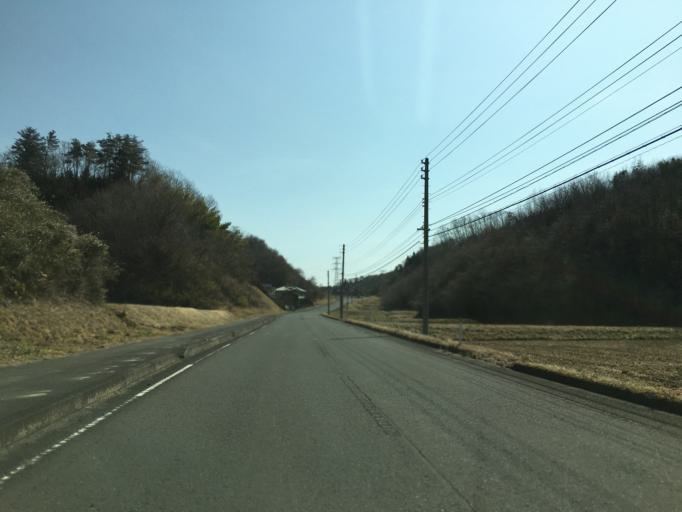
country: JP
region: Fukushima
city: Ishikawa
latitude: 37.0427
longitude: 140.4704
